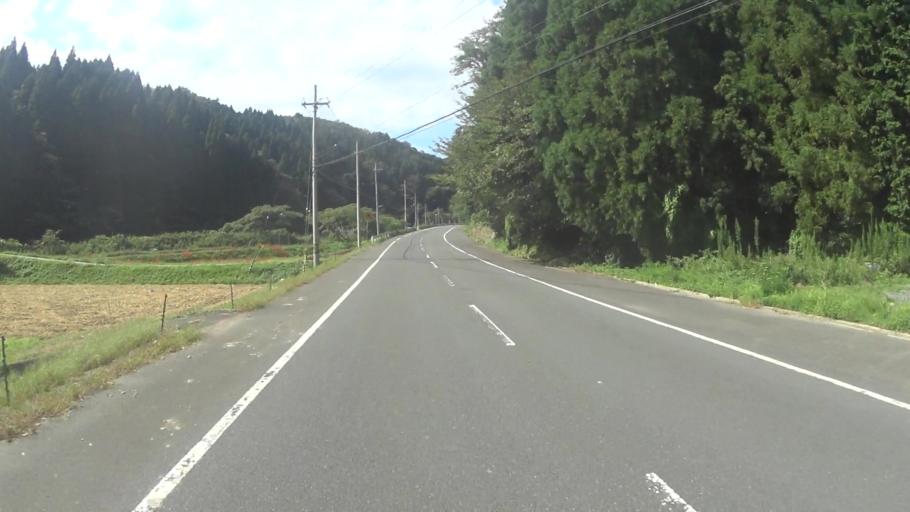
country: JP
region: Kyoto
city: Miyazu
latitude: 35.7328
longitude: 135.2579
